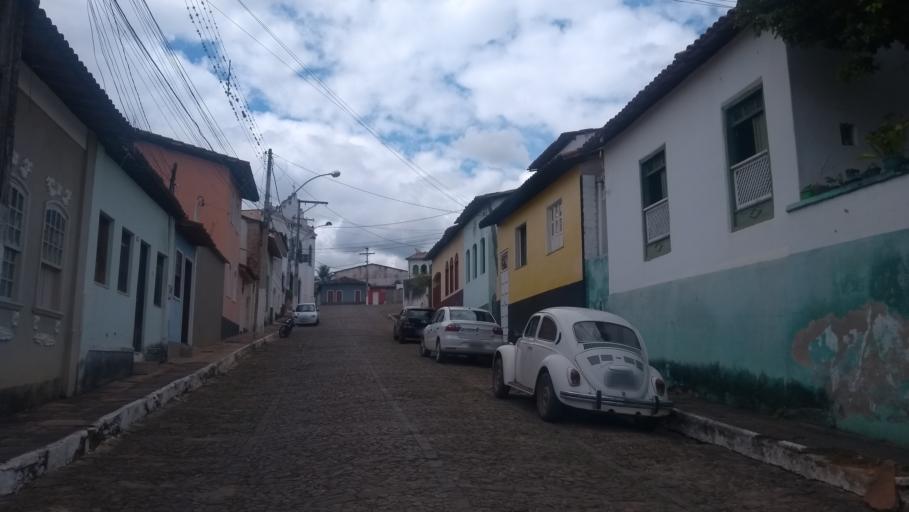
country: BR
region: Bahia
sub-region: Andarai
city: Vera Cruz
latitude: -12.5632
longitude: -41.3890
